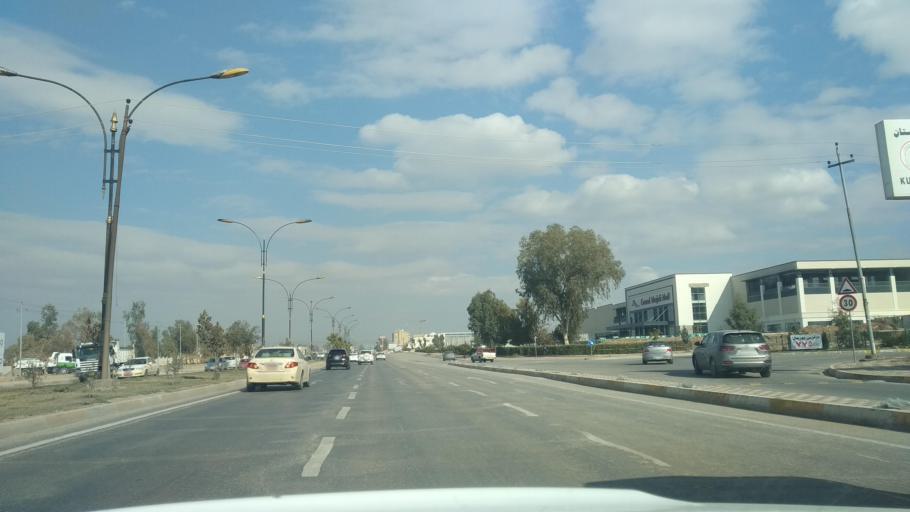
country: IQ
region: Arbil
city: Erbil
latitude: 36.2527
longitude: 44.0786
